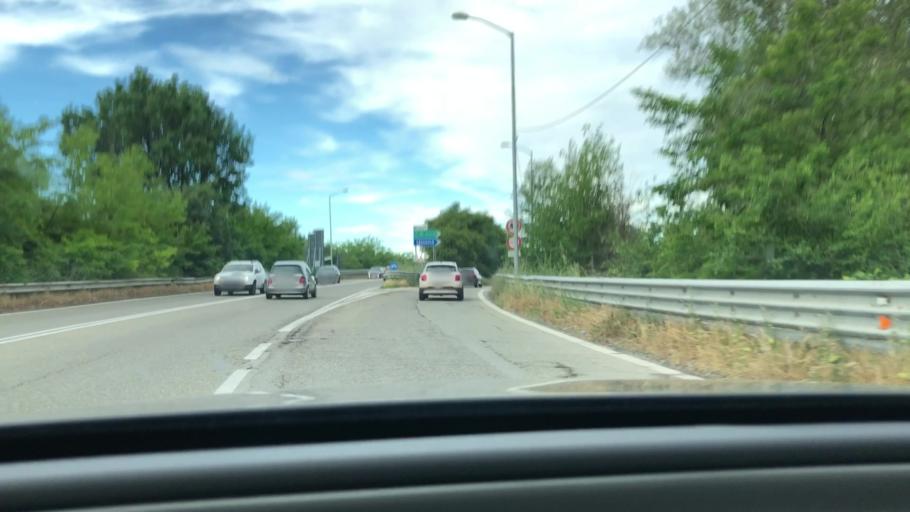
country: IT
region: Emilia-Romagna
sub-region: Provincia di Modena
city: Montale
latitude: 44.6012
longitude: 10.9309
